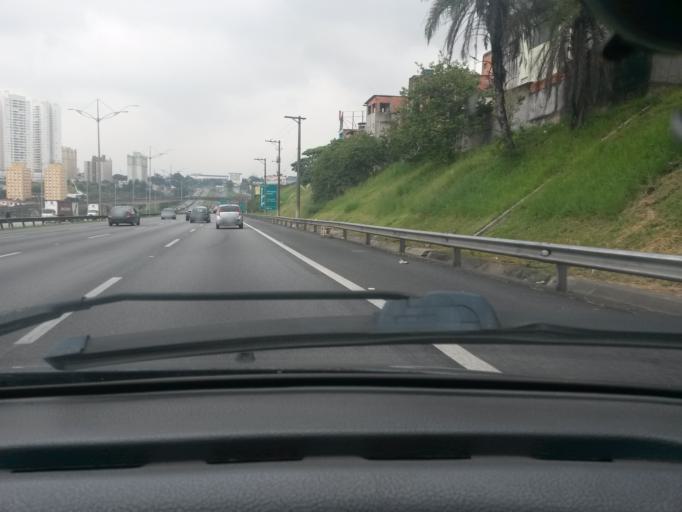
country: BR
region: Sao Paulo
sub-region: Sao Bernardo Do Campo
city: Sao Bernardo do Campo
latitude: -23.7032
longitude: -46.5617
